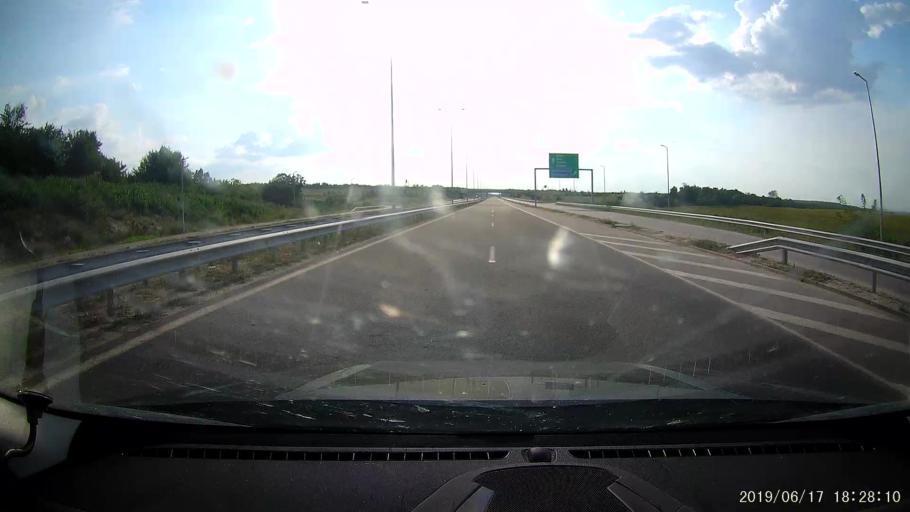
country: BG
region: Khaskovo
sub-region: Obshtina Dimitrovgrad
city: Dimitrovgrad
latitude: 42.0212
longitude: 25.5874
